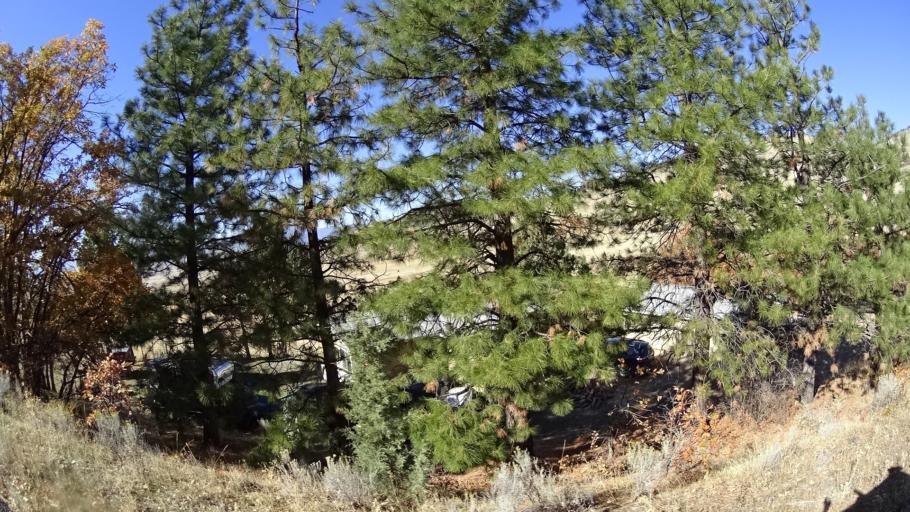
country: US
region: California
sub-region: Siskiyou County
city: Montague
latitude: 41.8290
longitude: -122.3429
